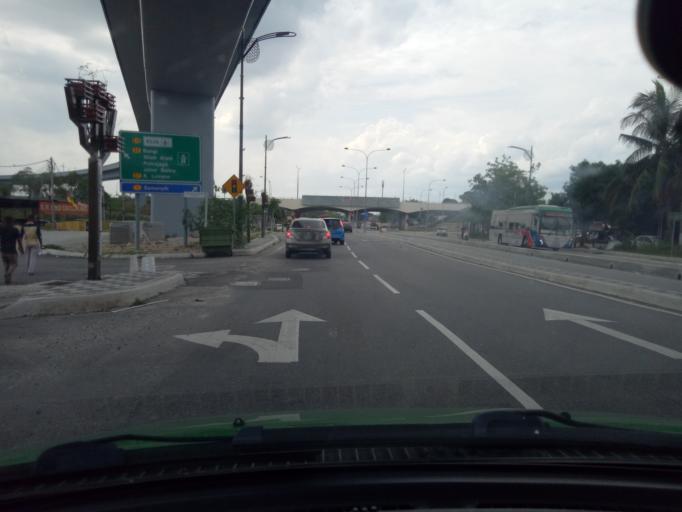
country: MY
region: Selangor
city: Kampong Baharu Balakong
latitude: 3.0022
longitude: 101.7829
